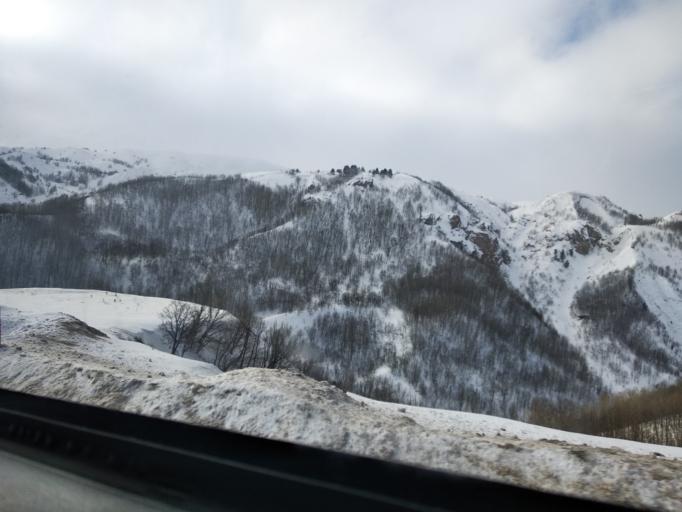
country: TR
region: Erzincan
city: Catalarmut
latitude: 39.8962
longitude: 39.3871
